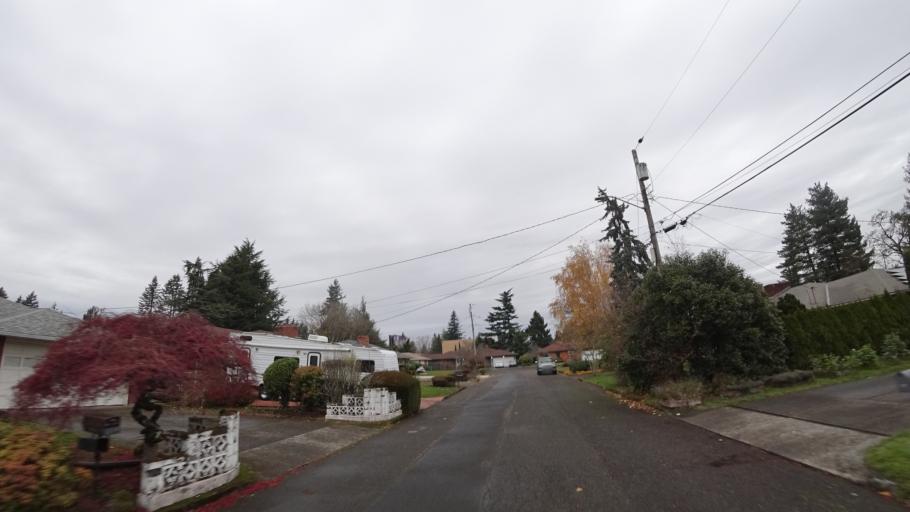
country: US
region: Oregon
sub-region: Multnomah County
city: Lents
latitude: 45.5320
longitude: -122.5434
